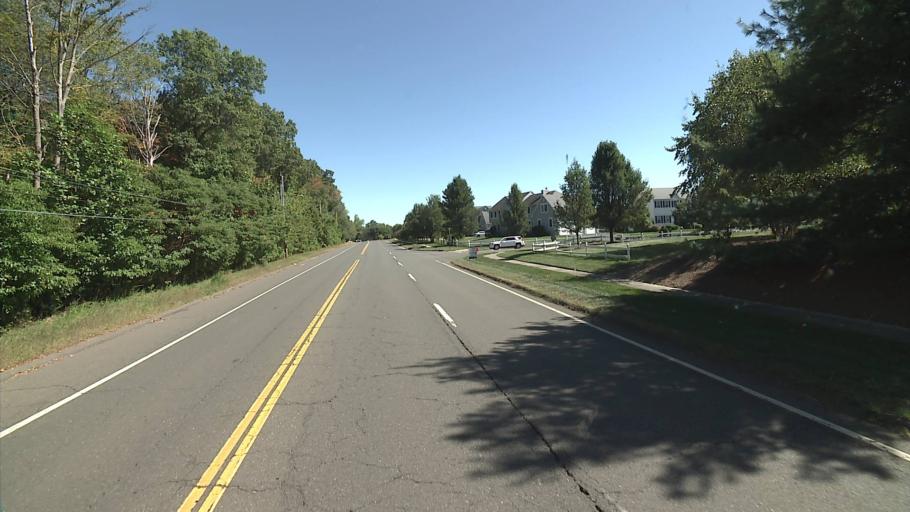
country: US
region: Connecticut
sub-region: New Haven County
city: Wallingford
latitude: 41.4937
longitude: -72.8490
